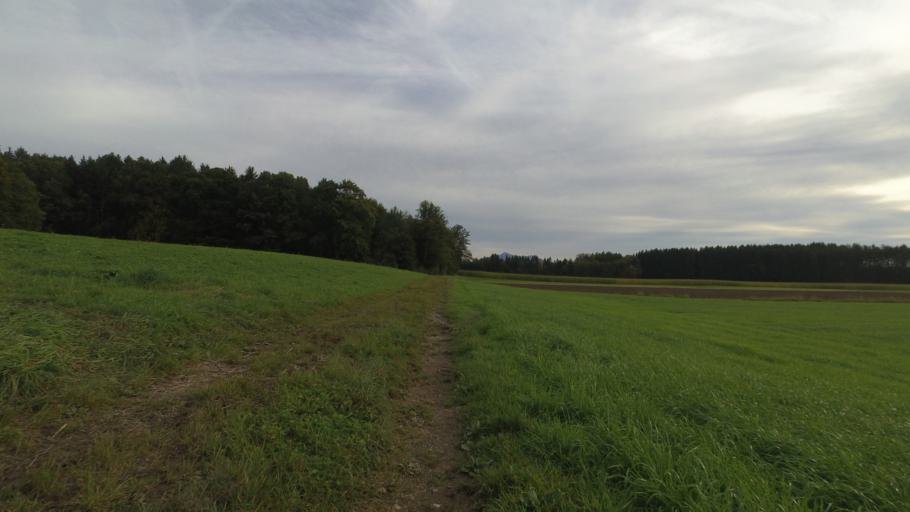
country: DE
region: Bavaria
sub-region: Upper Bavaria
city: Chieming
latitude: 47.9227
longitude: 12.5435
